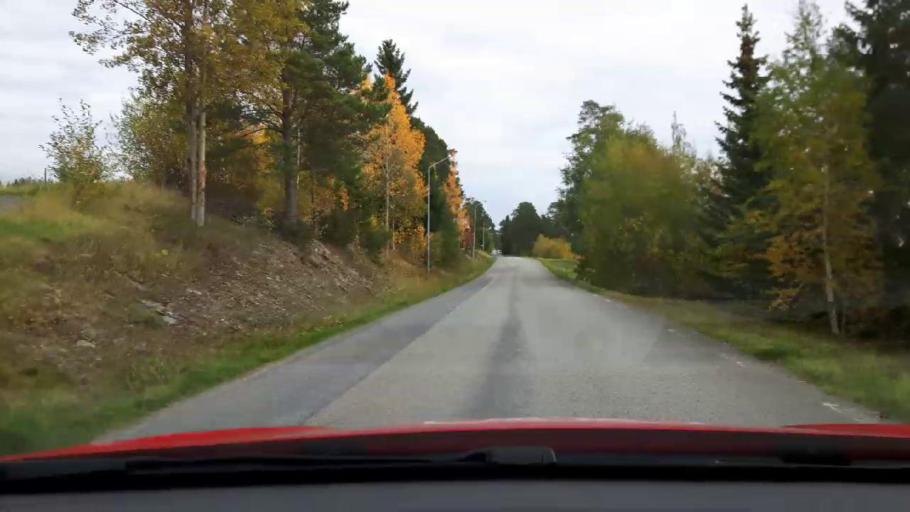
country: SE
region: Jaemtland
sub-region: Krokoms Kommun
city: Valla
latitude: 63.2577
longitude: 14.0174
